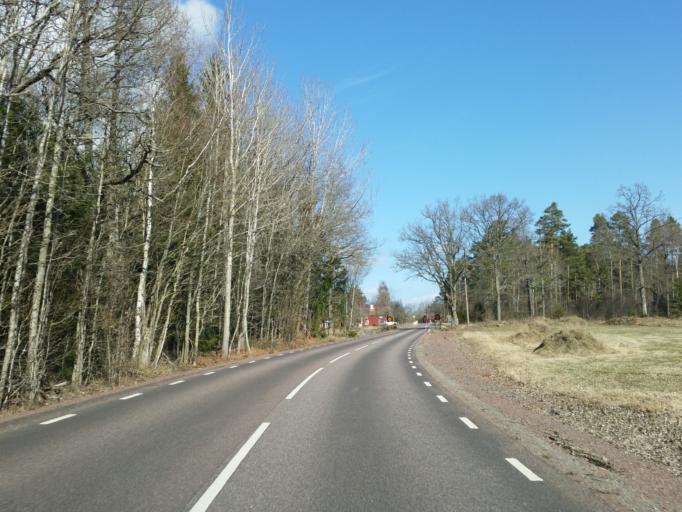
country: SE
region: Kalmar
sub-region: Monsteras Kommun
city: Timmernabben
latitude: 56.8978
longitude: 16.4295
